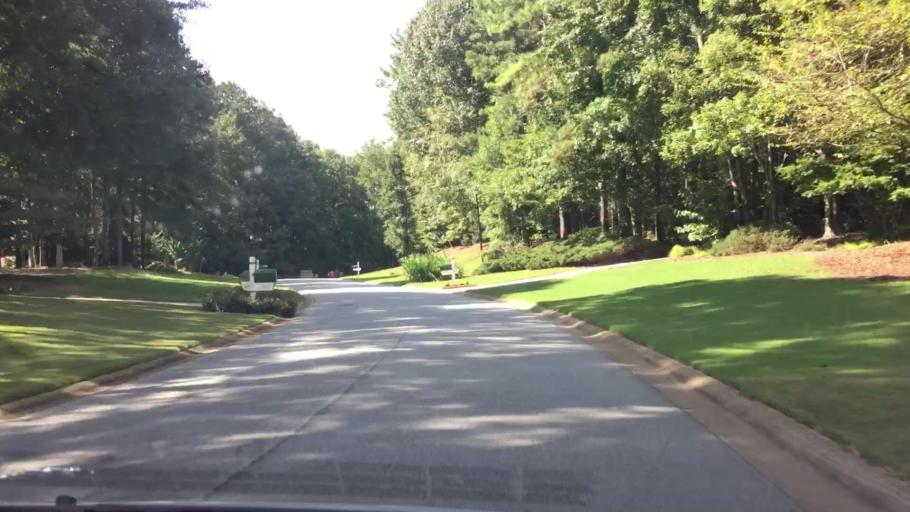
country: US
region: Georgia
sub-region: Coweta County
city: Senoia
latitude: 33.3586
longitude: -84.5191
